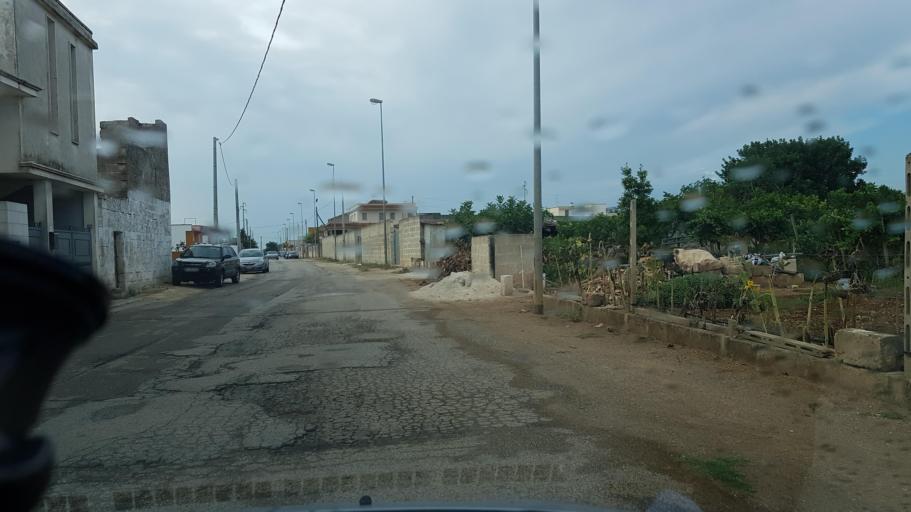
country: IT
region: Apulia
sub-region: Provincia di Brindisi
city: Torre Santa Susanna
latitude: 40.4690
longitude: 17.7330
